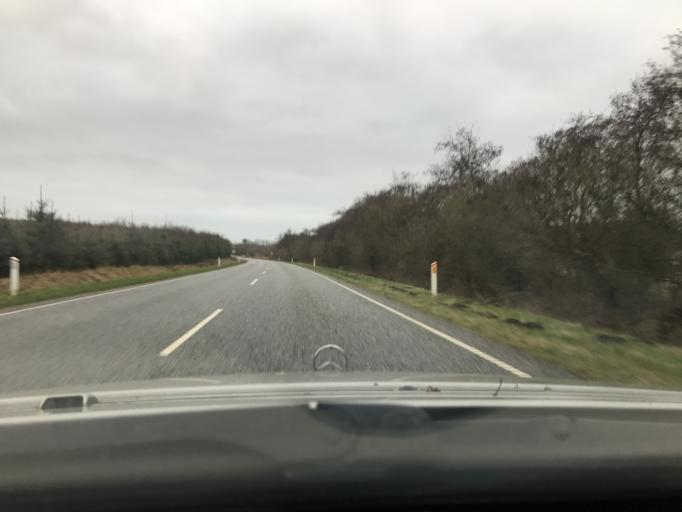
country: DK
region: South Denmark
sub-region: Tonder Kommune
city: Sherrebek
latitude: 55.1713
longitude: 8.7644
